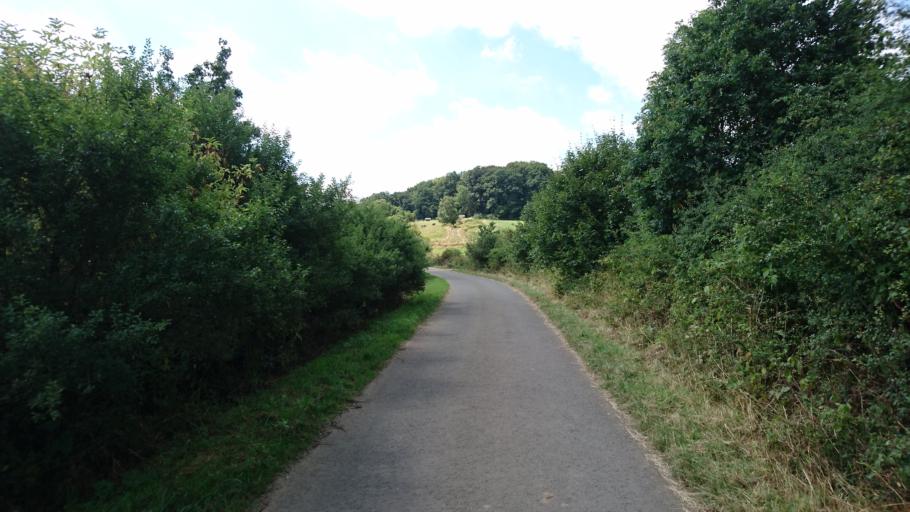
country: DE
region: Hesse
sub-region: Regierungsbezirk Giessen
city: Breitscheid
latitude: 50.6782
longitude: 8.2323
